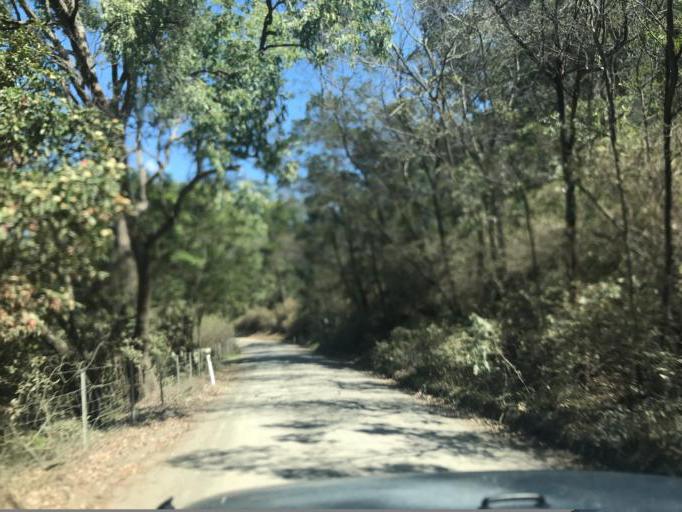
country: AU
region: New South Wales
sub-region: Hawkesbury
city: Pitt Town
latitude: -33.4239
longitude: 150.8948
